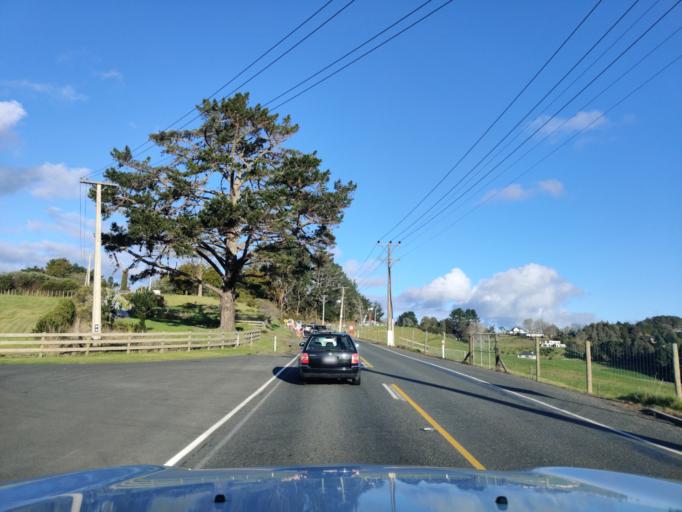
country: NZ
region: Auckland
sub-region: Auckland
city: Red Hill
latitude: -36.9673
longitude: 174.9838
